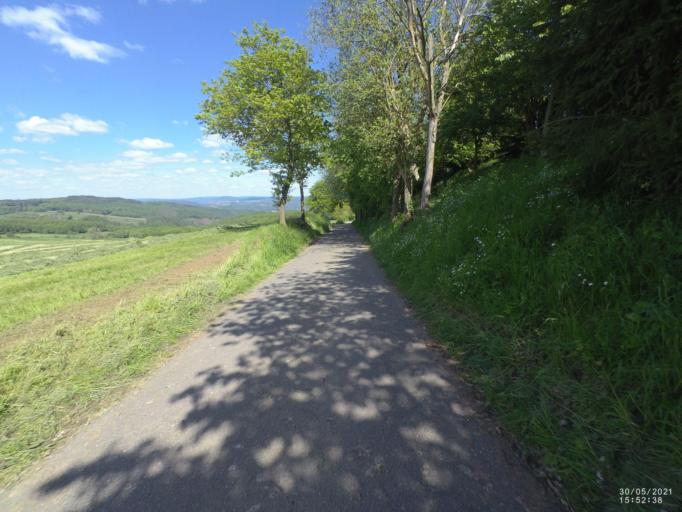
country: DE
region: Rheinland-Pfalz
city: Waldesch
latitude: 50.2672
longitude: 7.5481
